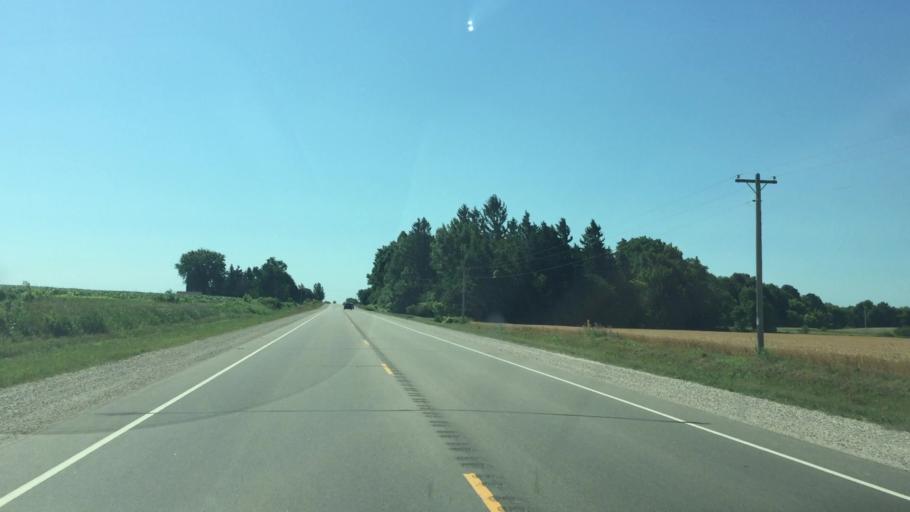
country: US
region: Wisconsin
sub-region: Calumet County
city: Chilton
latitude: 43.9956
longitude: -88.1285
